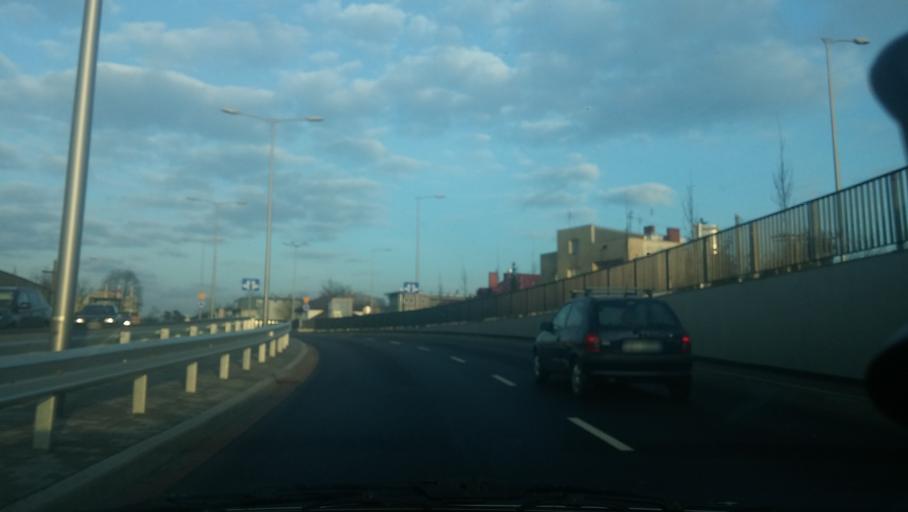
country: PL
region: Masovian Voivodeship
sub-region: Warszawa
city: Wawer
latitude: 52.2055
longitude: 21.1690
